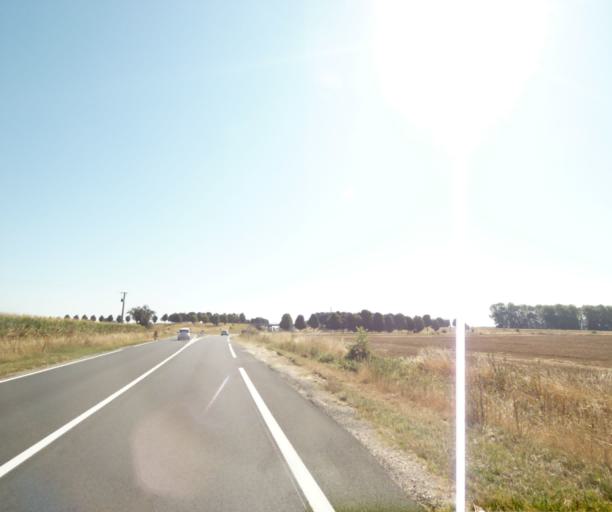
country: FR
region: Ile-de-France
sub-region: Departement de Seine-et-Marne
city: Moissy-Cramayel
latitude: 48.6311
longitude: 2.6245
